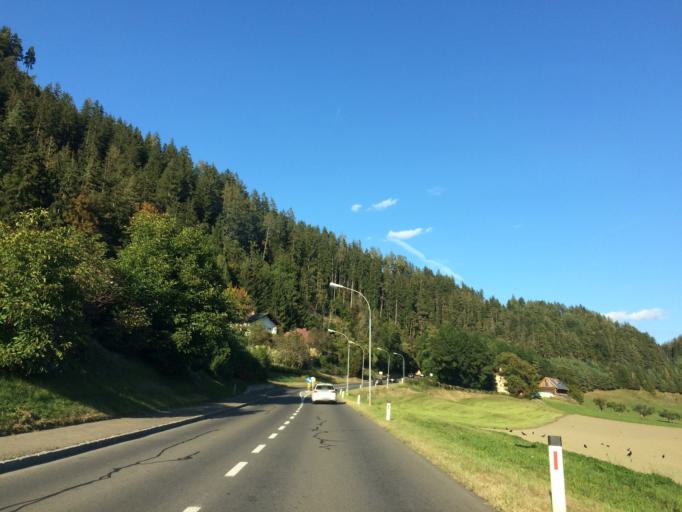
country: AT
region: Styria
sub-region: Politischer Bezirk Leoben
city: Leoben
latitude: 47.3628
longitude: 15.0671
